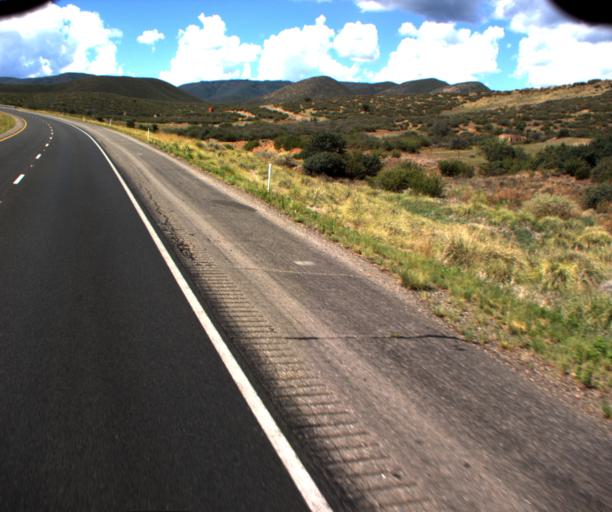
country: US
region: Arizona
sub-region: Yavapai County
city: Mayer
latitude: 34.4613
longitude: -112.2711
